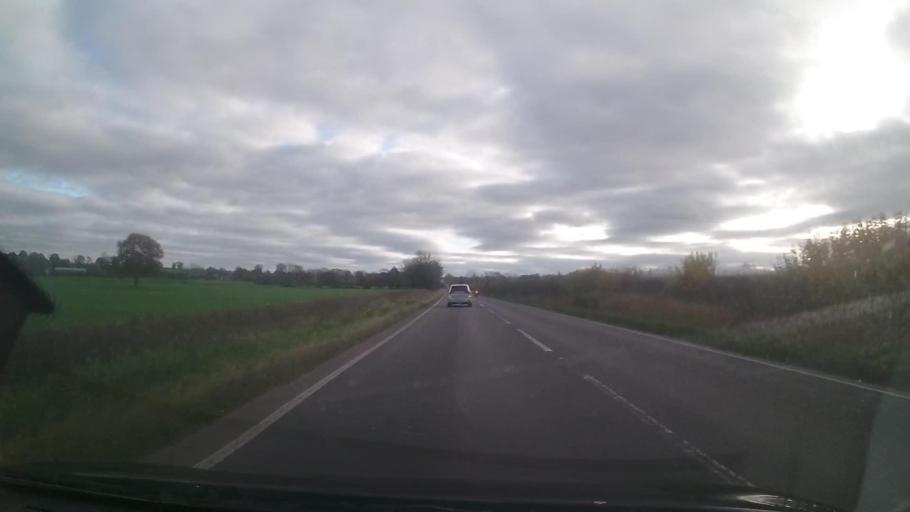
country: GB
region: England
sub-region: Shropshire
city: Stoke upon Tern
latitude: 52.8940
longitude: -2.5556
